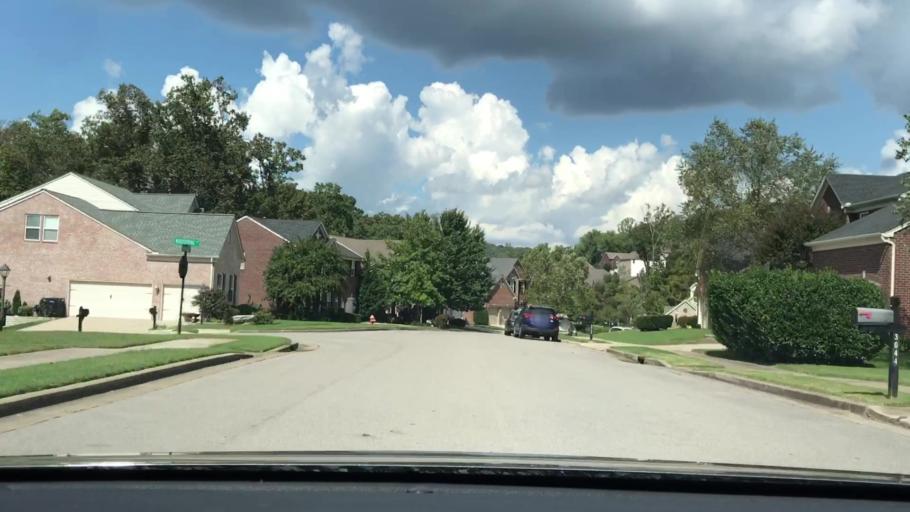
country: US
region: Tennessee
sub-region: Williamson County
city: Brentwood Estates
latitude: 36.0148
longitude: -86.7126
